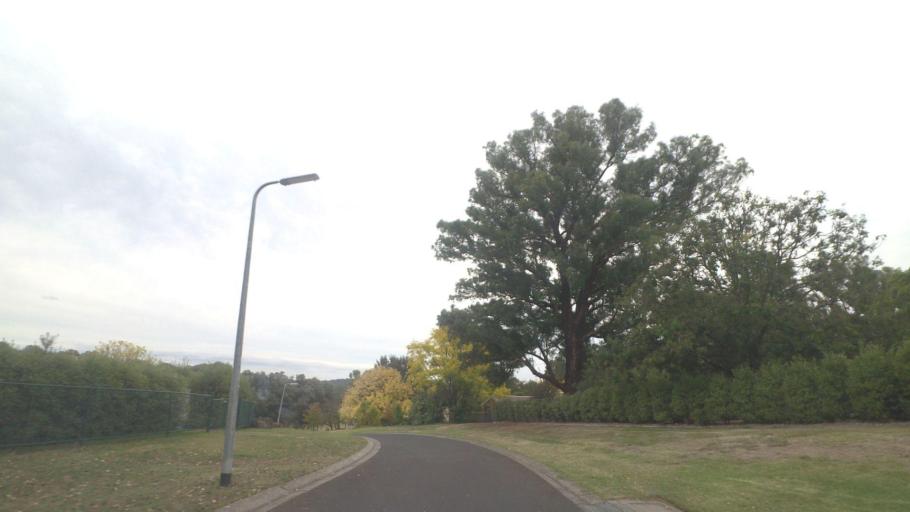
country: AU
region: Victoria
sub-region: Nillumbik
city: North Warrandyte
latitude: -37.7418
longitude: 145.1858
